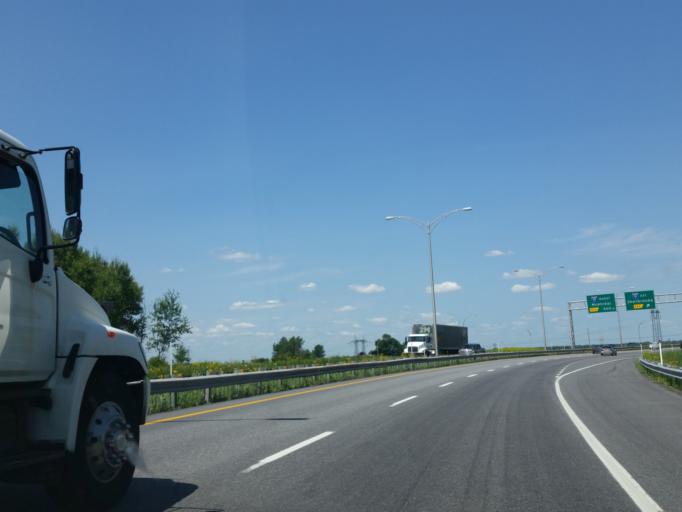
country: CA
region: Quebec
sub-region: Monteregie
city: Carignan
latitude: 45.4036
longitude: -73.3140
